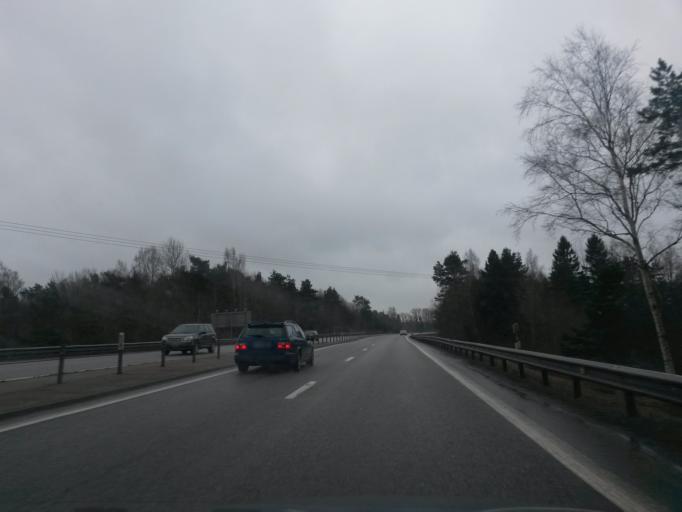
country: SE
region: Vaestra Goetaland
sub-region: Vanersborgs Kommun
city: Vanersborg
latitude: 58.3531
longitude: 12.3145
